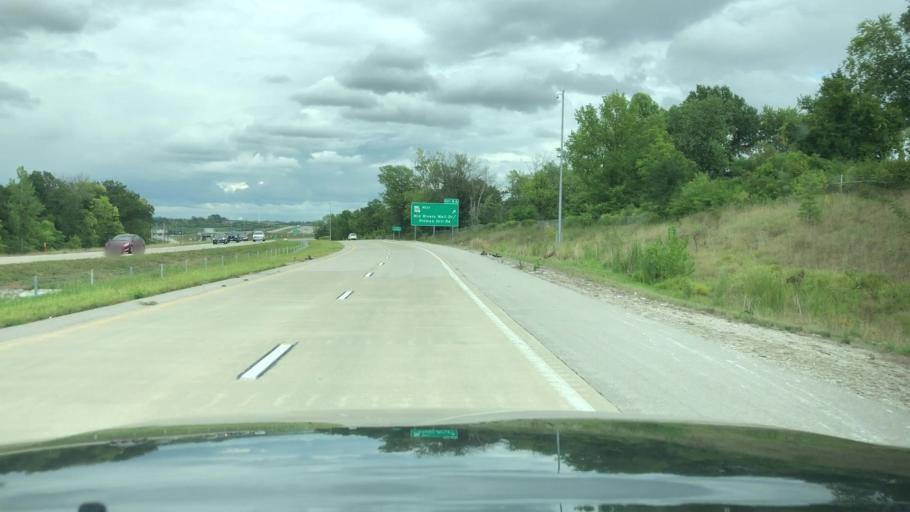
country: US
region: Missouri
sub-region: Saint Charles County
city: Cottleville
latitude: 38.7342
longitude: -90.6451
